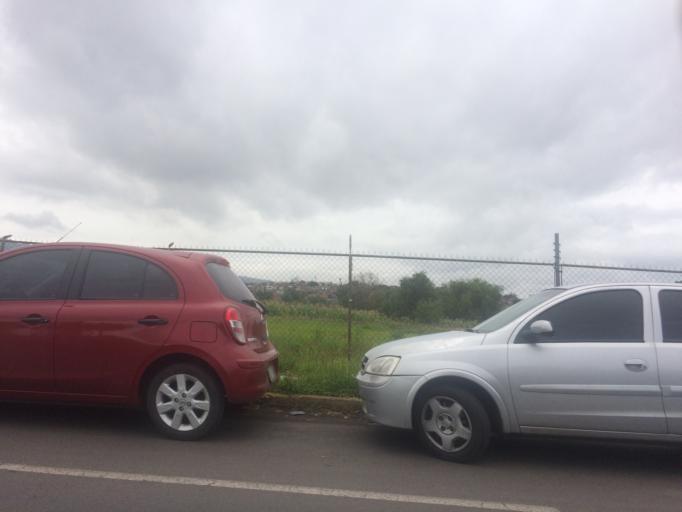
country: MX
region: Michoacan
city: Morelia
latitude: 19.7172
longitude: -101.1807
